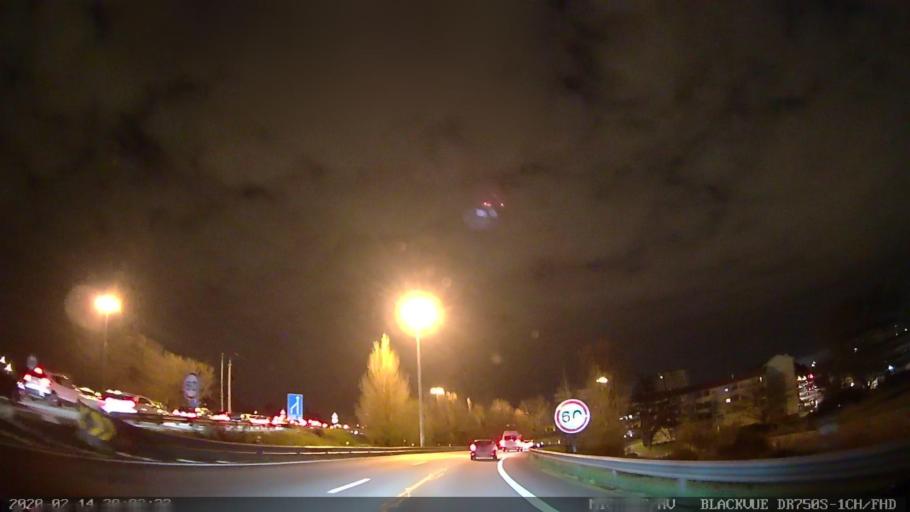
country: PT
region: Porto
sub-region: Maia
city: Pedroucos
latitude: 41.1731
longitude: -8.5953
